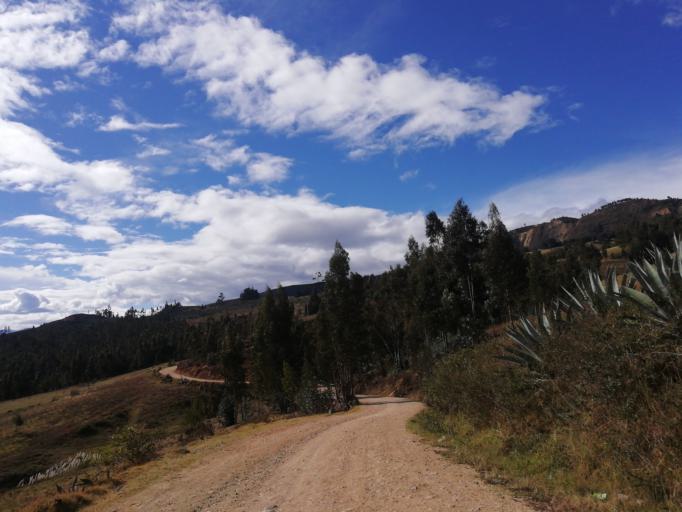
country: CO
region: Boyaca
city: Gameza
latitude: 5.8056
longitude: -72.8080
